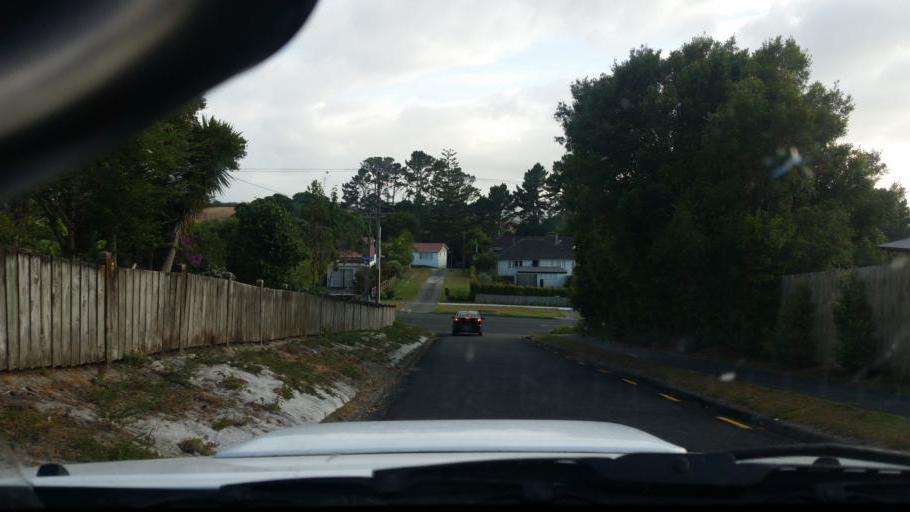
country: NZ
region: Northland
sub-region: Kaipara District
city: Dargaville
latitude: -35.9315
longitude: 173.8550
